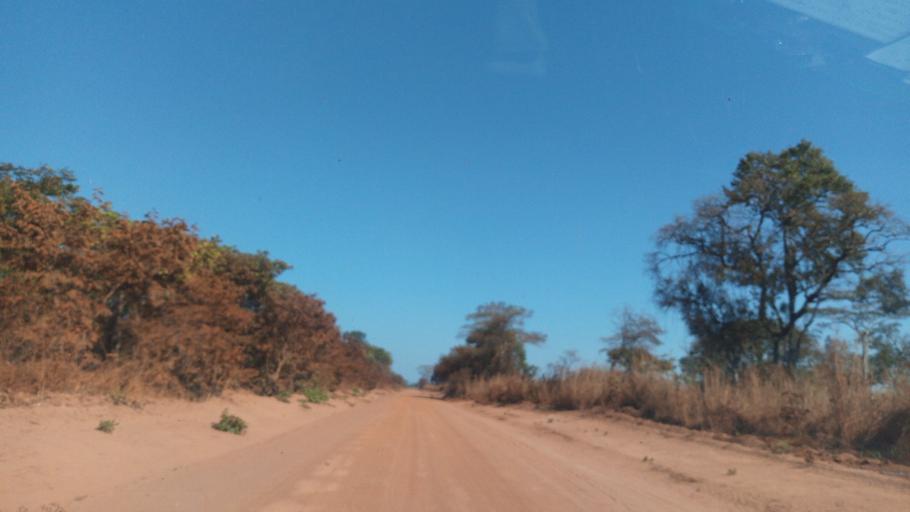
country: ZM
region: Luapula
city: Mwense
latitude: -10.7545
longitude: 28.3130
